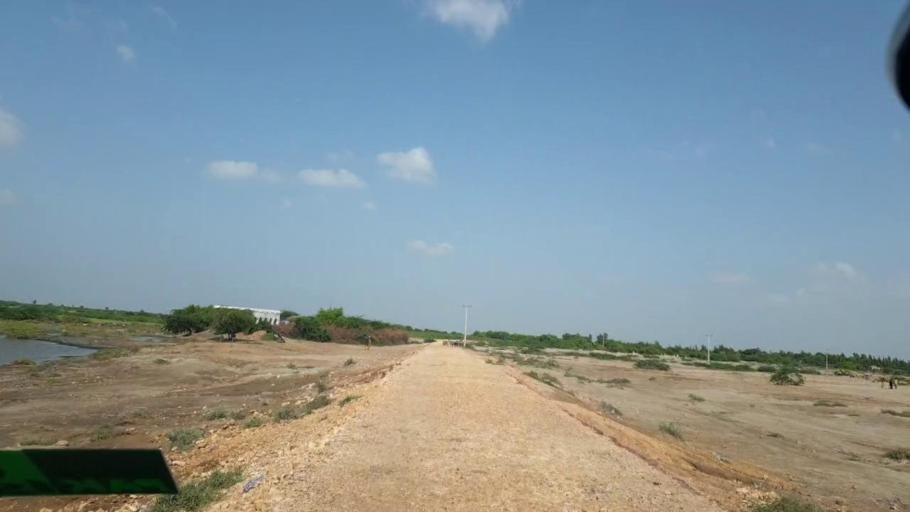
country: PK
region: Sindh
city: Tando Bago
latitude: 24.6669
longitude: 69.2050
